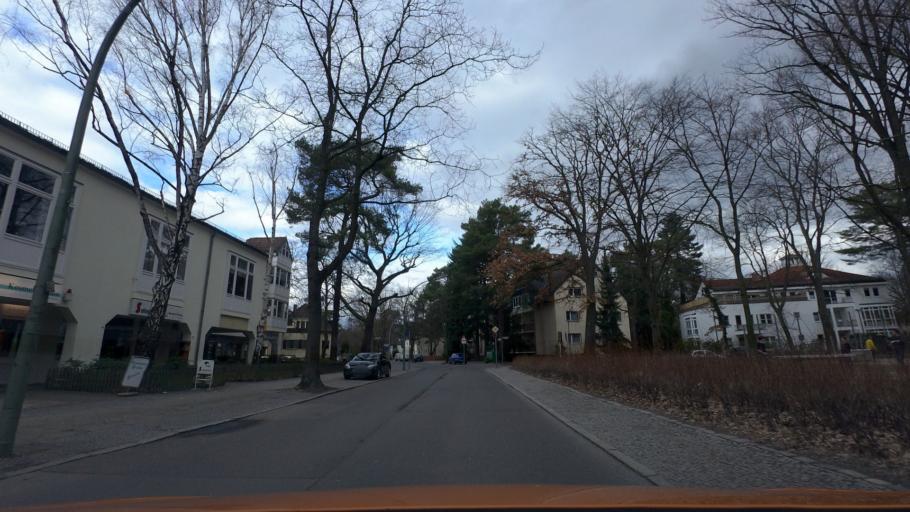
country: DE
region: Berlin
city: Konradshohe
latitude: 52.5853
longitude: 13.2270
